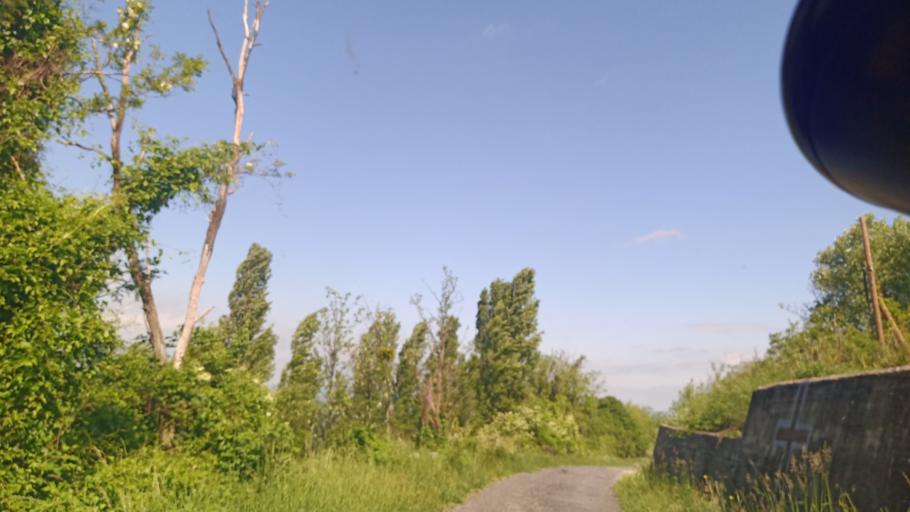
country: HU
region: Zala
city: Pacsa
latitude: 46.6604
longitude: 17.0623
